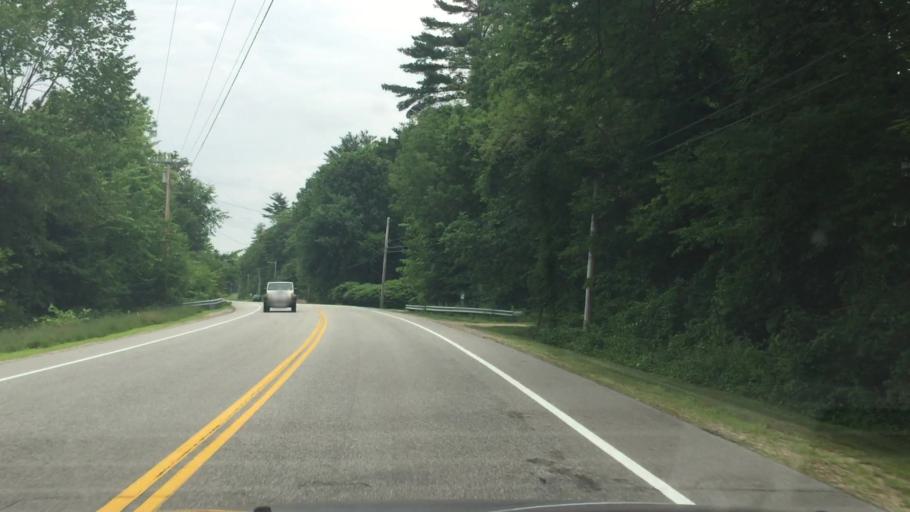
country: US
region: New Hampshire
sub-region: Carroll County
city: Sandwich
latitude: 43.8022
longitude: -71.3584
